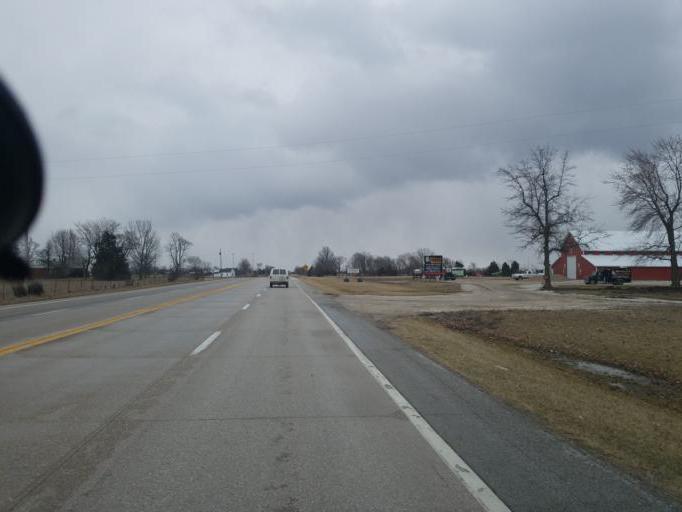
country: US
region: Missouri
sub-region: Macon County
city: Macon
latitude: 39.7776
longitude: -92.4775
